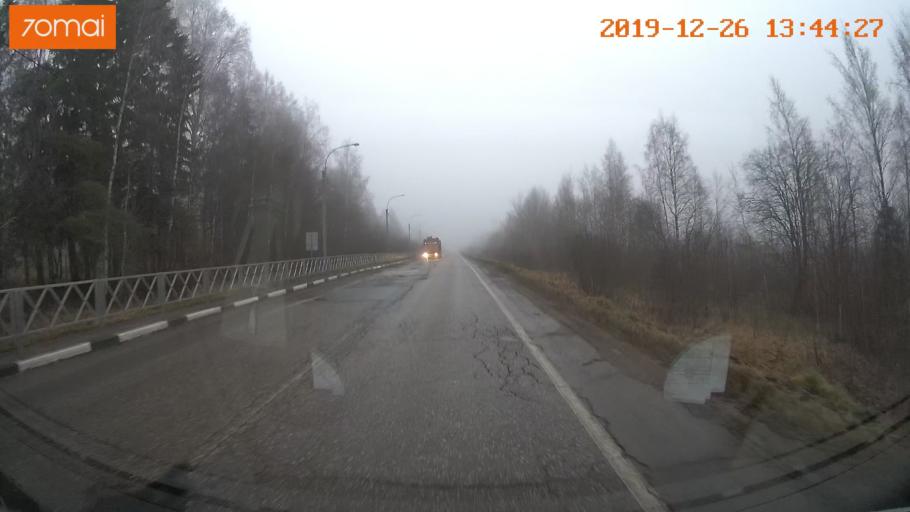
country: RU
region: Vologda
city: Sheksna
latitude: 58.7019
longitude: 38.5066
